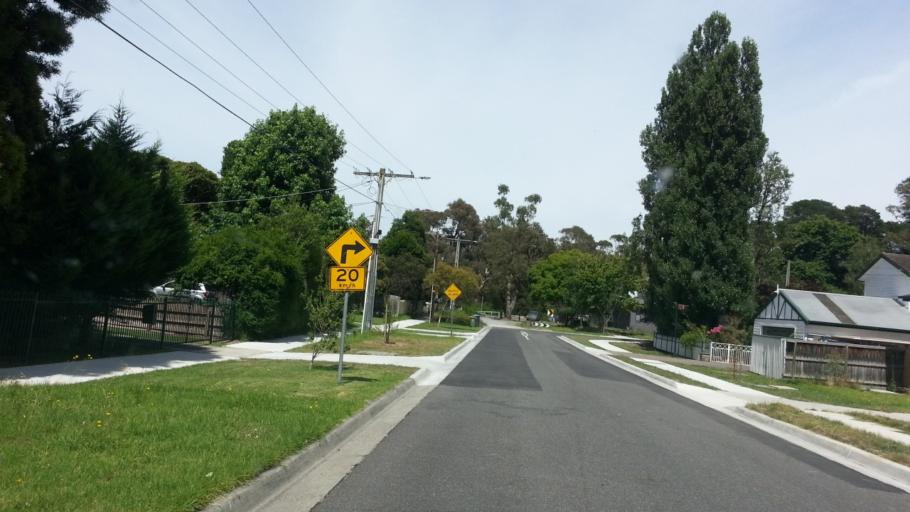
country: AU
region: Victoria
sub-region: Knox
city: Boronia
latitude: -37.8674
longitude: 145.2770
